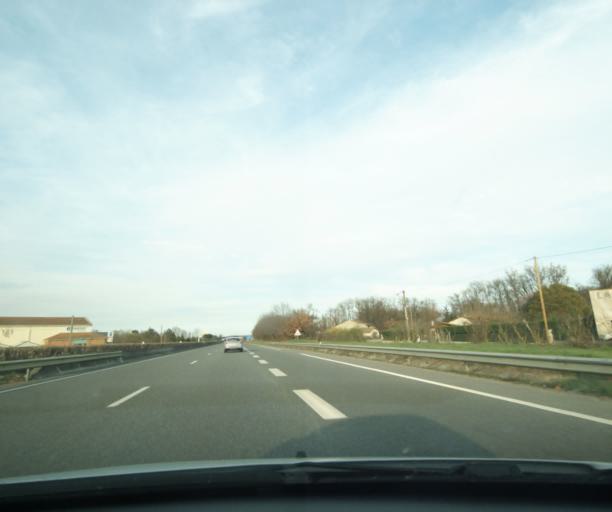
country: FR
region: Midi-Pyrenees
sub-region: Departement de la Haute-Garonne
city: Carbonne
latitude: 43.3211
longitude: 1.2197
